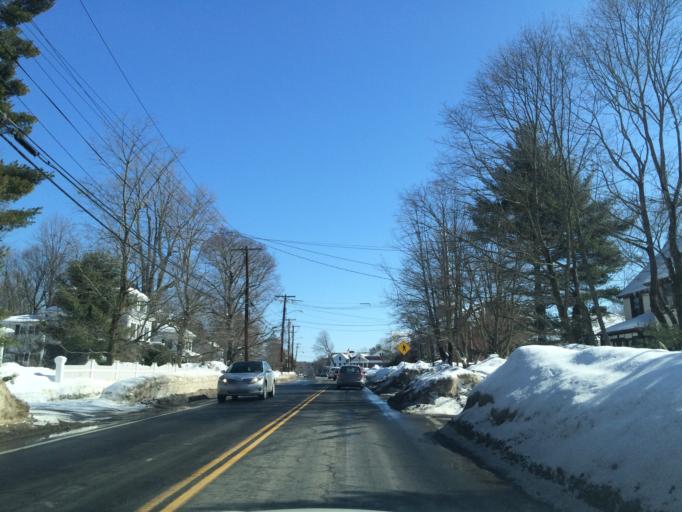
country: US
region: Massachusetts
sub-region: Norfolk County
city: Needham
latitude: 42.2802
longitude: -71.2428
